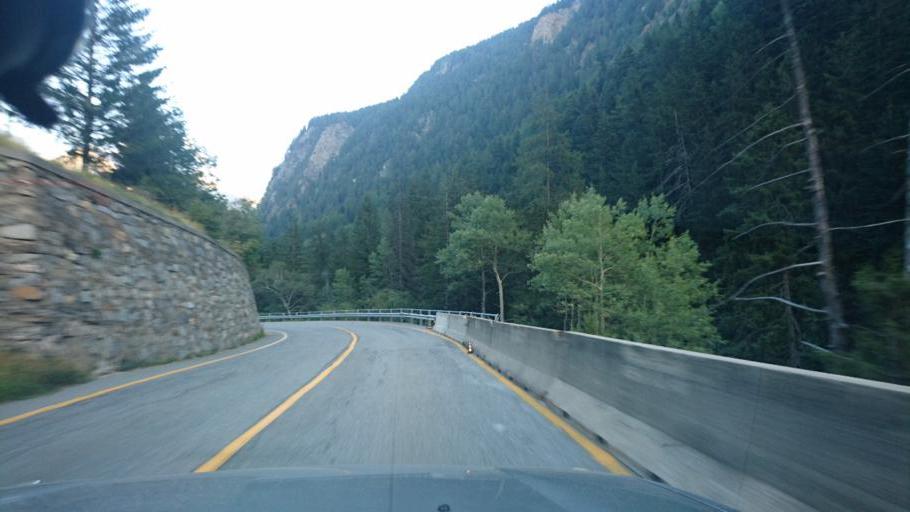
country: IT
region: Aosta Valley
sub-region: Valle d'Aosta
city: La Thuile
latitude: 45.7393
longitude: 6.9625
